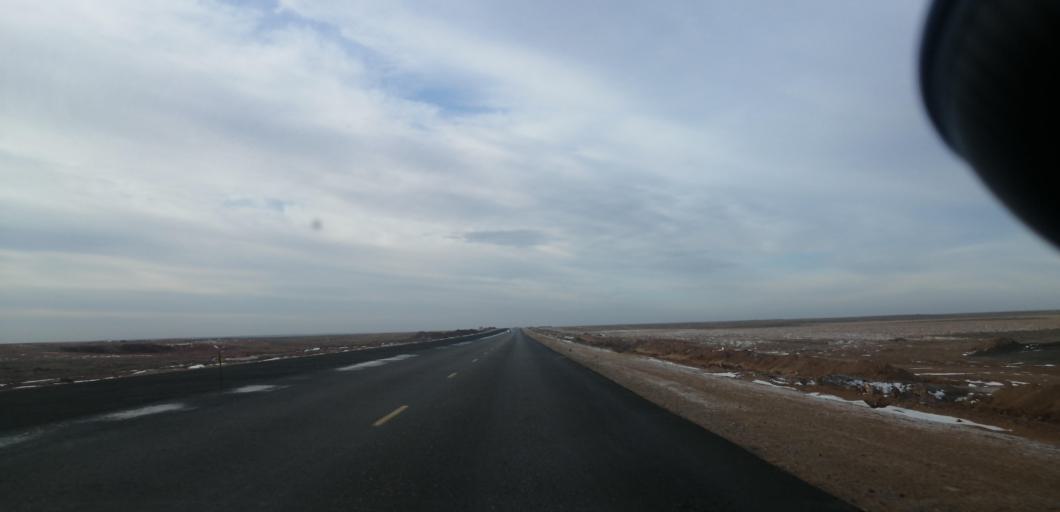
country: KZ
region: Qaraghandy
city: Saryshaghan
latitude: 46.4372
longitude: 73.9683
